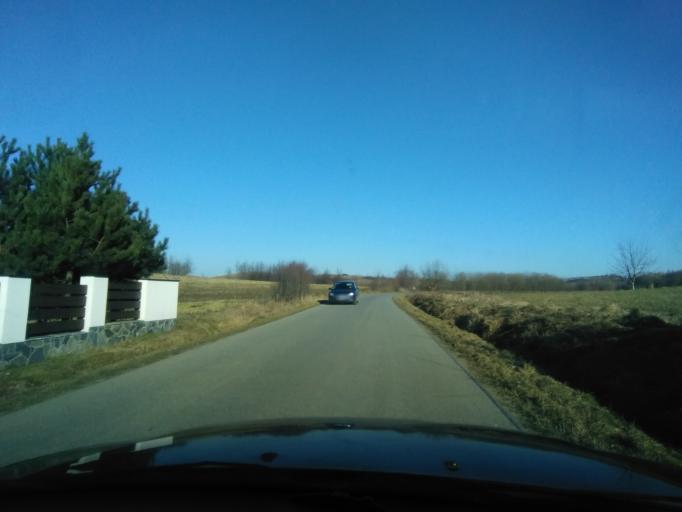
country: PL
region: Subcarpathian Voivodeship
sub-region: Powiat krosnienski
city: Rymanow
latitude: 49.5814
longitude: 21.8834
